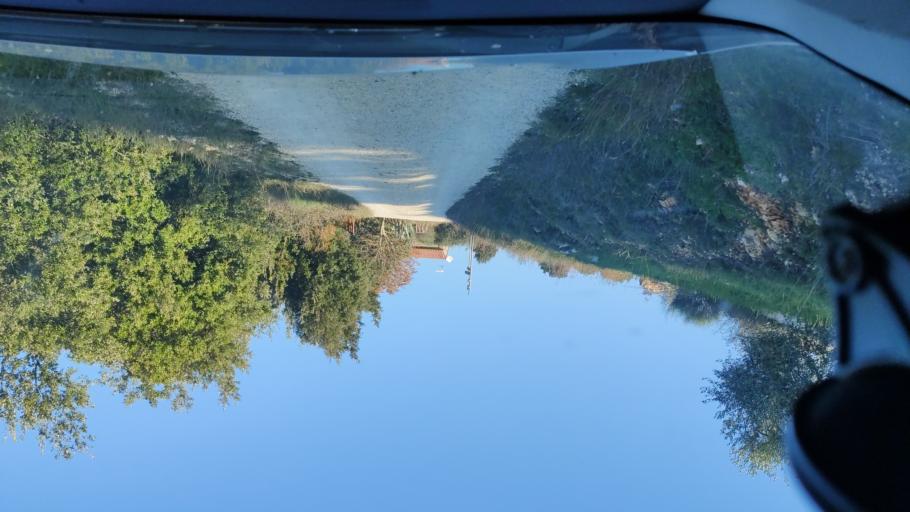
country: IT
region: Umbria
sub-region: Provincia di Terni
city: Avigliano Umbro
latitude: 42.6056
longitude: 12.4316
